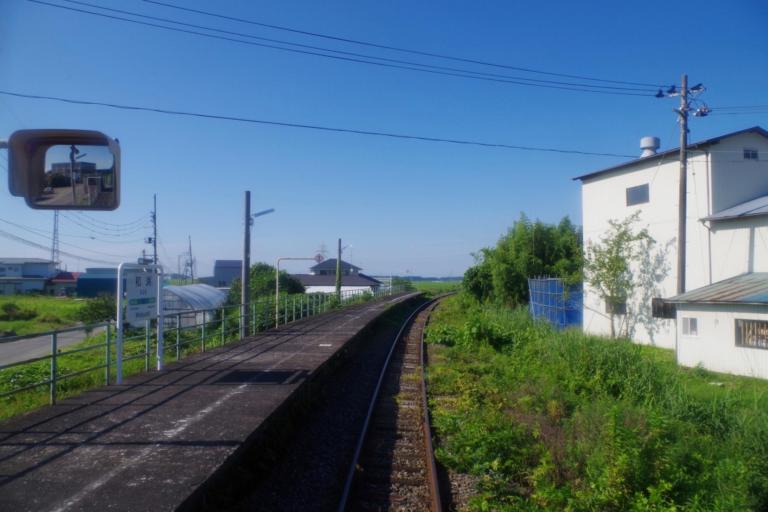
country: JP
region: Miyagi
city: Wakuya
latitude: 38.5261
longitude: 141.2206
